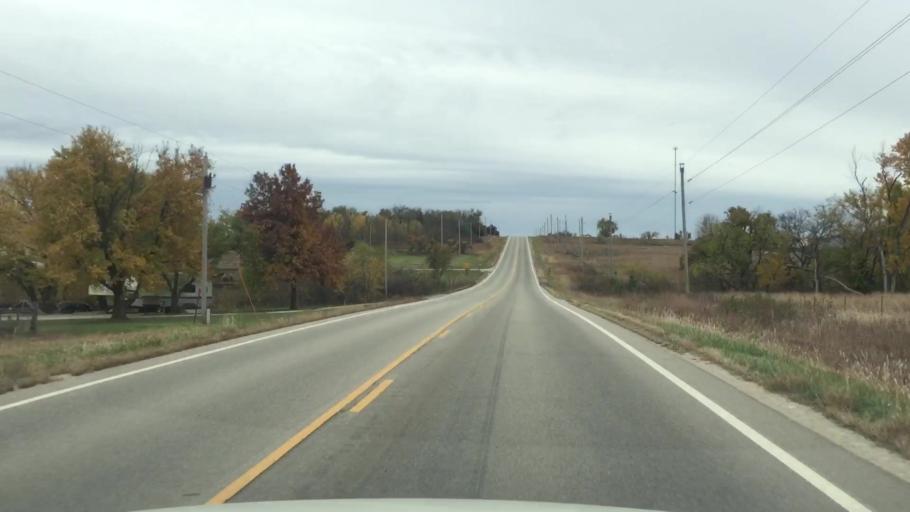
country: US
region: Kansas
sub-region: Pottawatomie County
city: Wamego
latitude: 39.1113
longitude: -96.2894
